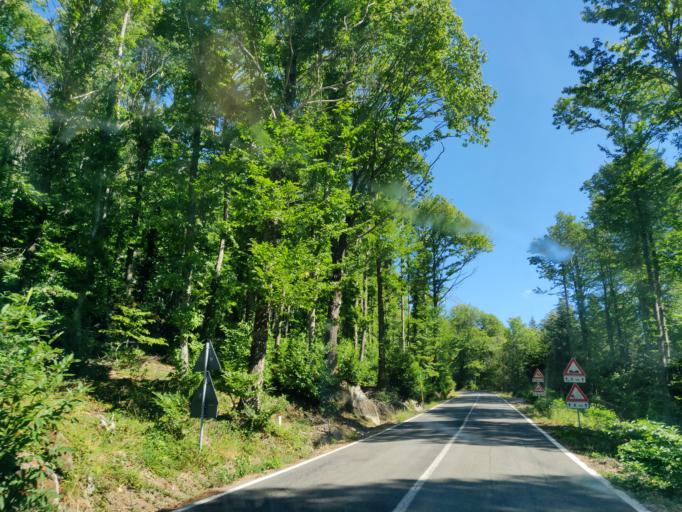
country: IT
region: Tuscany
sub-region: Provincia di Siena
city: Abbadia San Salvatore
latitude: 42.8980
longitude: 11.6487
